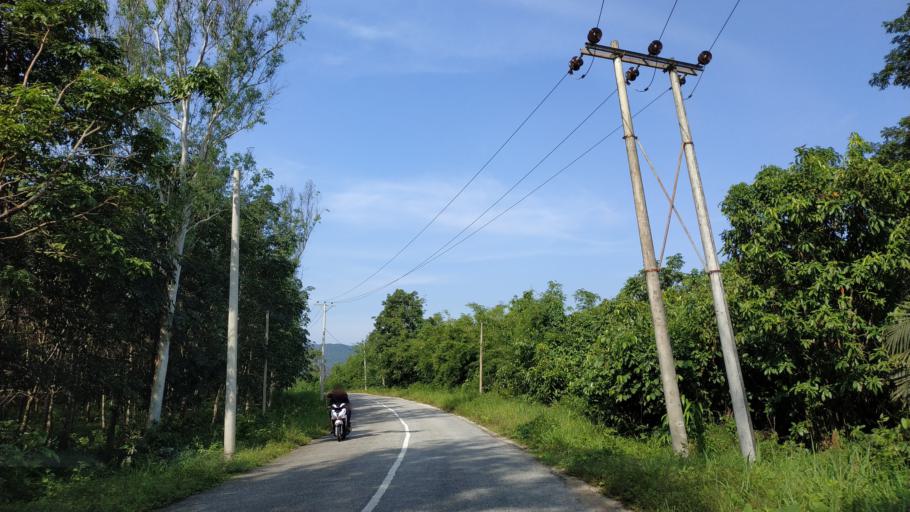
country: MM
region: Tanintharyi
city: Dawei
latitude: 14.5983
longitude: 98.0823
